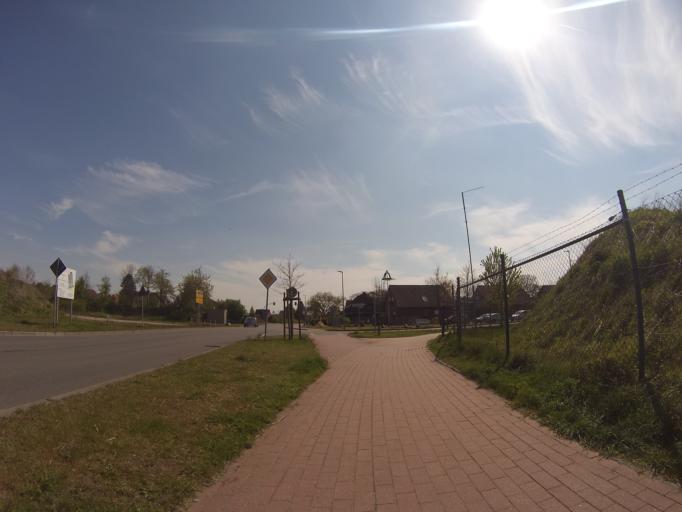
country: DE
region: Lower Saxony
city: Emlichheim
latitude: 52.6168
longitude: 6.8735
